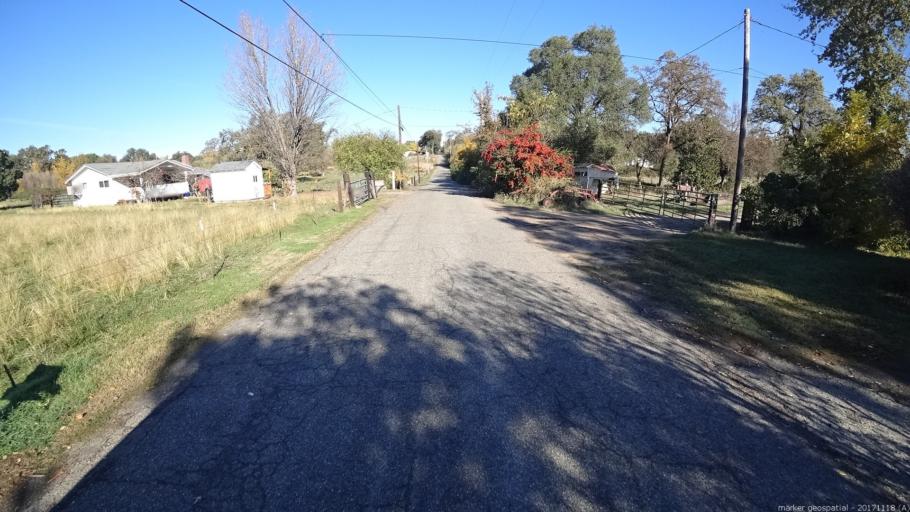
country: US
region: California
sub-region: Shasta County
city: Cottonwood
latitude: 40.3798
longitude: -122.3072
